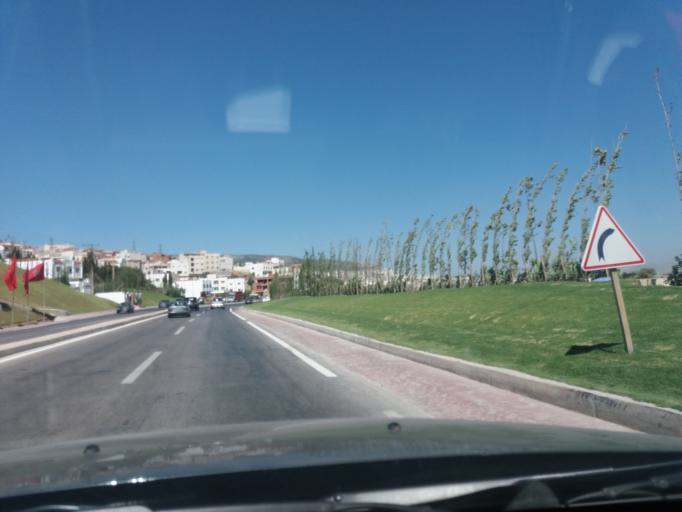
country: MA
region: Tanger-Tetouan
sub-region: Tetouan
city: Saddina
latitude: 35.5616
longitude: -5.4325
